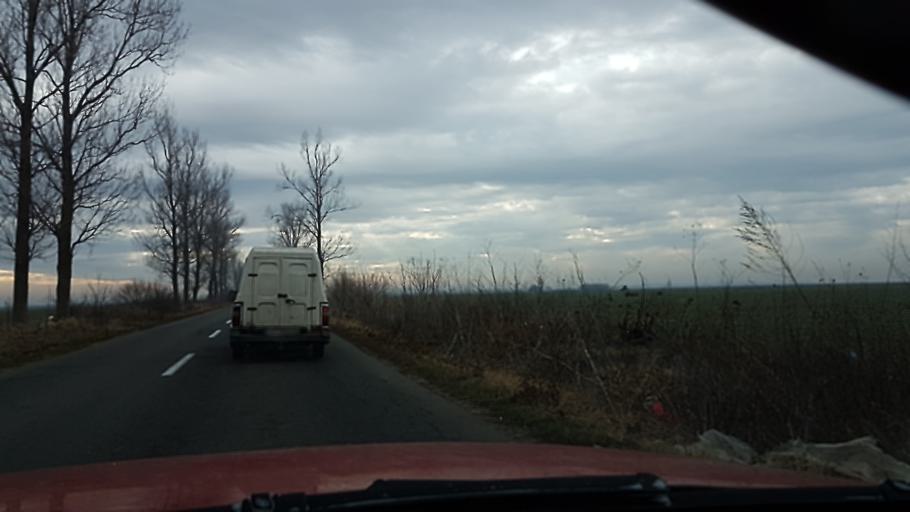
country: RO
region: Giurgiu
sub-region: Comuna Herasti
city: Herasti
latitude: 44.2359
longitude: 26.3604
